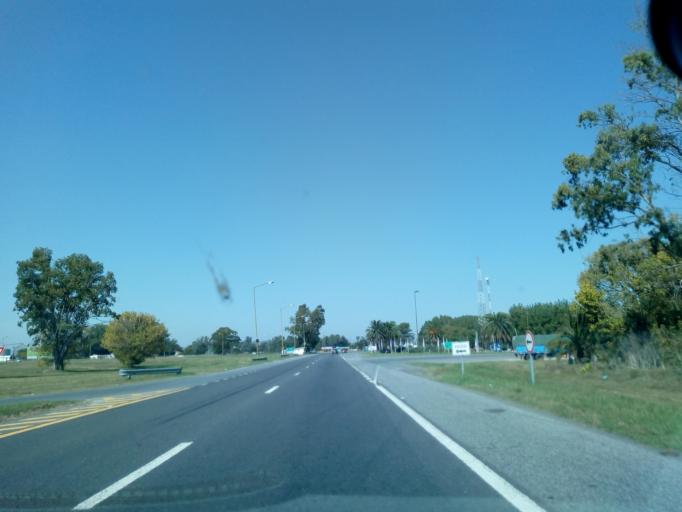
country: AR
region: Buenos Aires
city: Maipu
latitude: -37.0793
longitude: -57.8323
